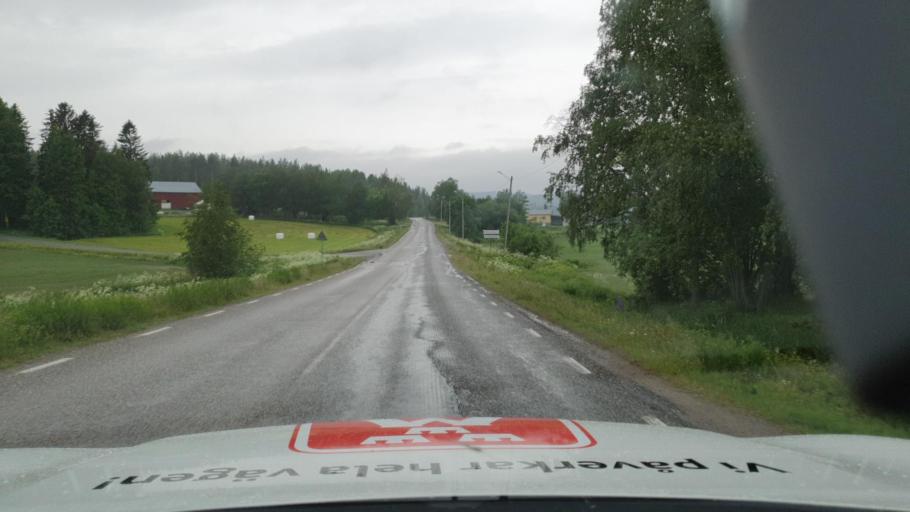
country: SE
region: Vaesterbotten
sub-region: Nordmalings Kommun
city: Nordmaling
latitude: 63.7951
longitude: 19.5265
